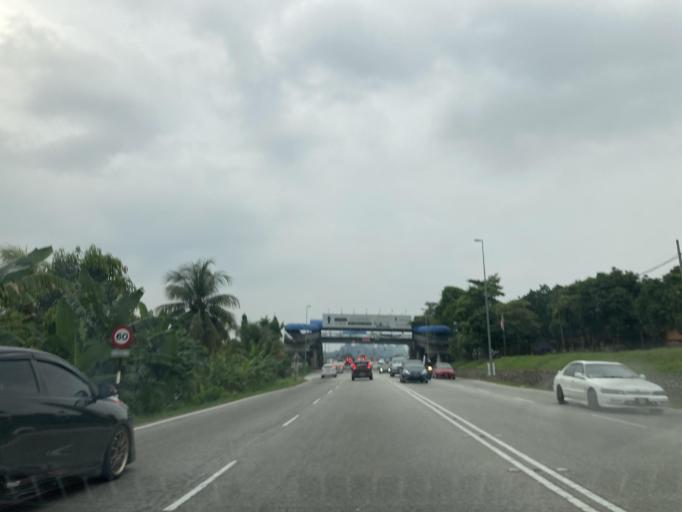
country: MY
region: Selangor
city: Kuang
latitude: 3.2063
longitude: 101.5415
